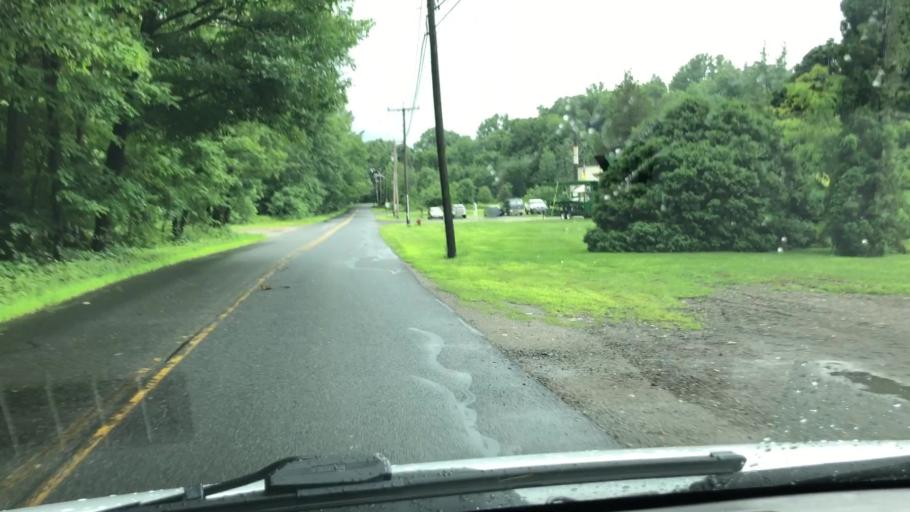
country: US
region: Massachusetts
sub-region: Hampshire County
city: Williamsburg
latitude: 42.3597
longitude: -72.7014
